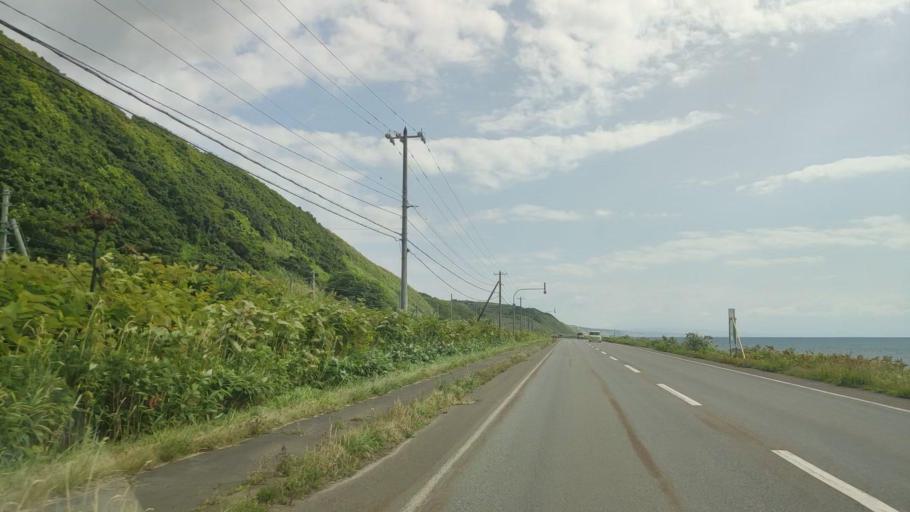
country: JP
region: Hokkaido
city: Rumoi
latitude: 44.1084
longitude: 141.6592
